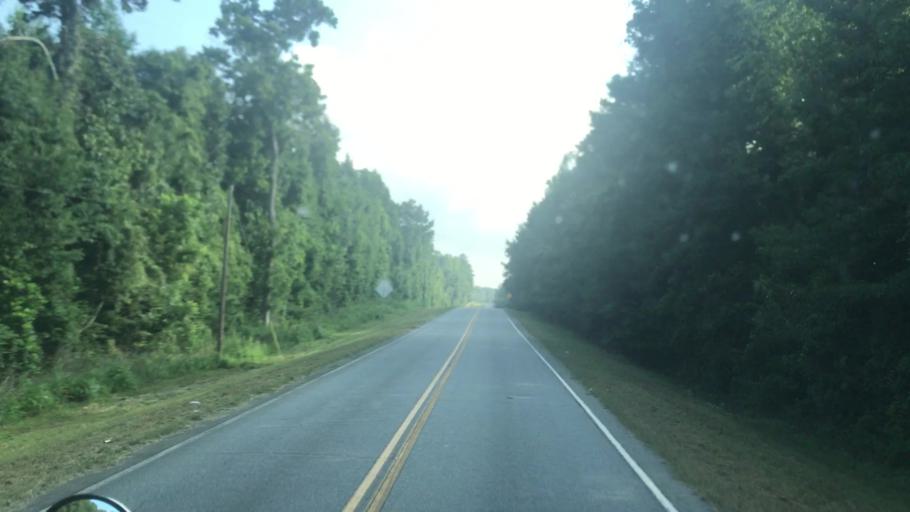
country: US
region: Florida
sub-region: Gadsden County
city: Havana
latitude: 30.7206
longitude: -84.4878
